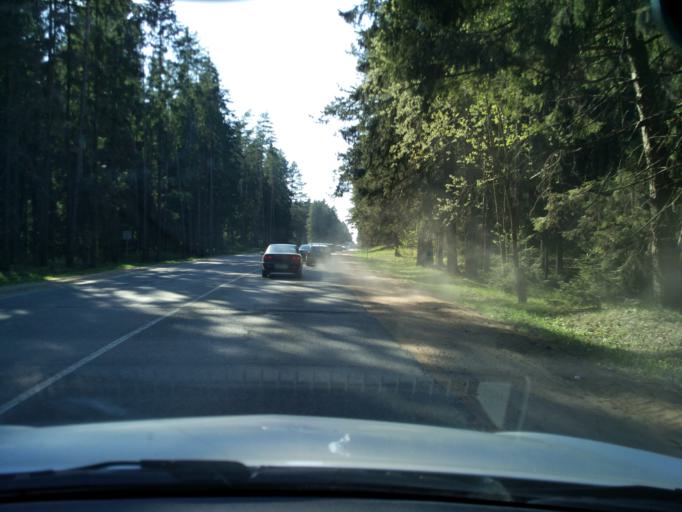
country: BY
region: Minsk
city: Borovlyany
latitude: 53.9611
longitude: 27.6928
